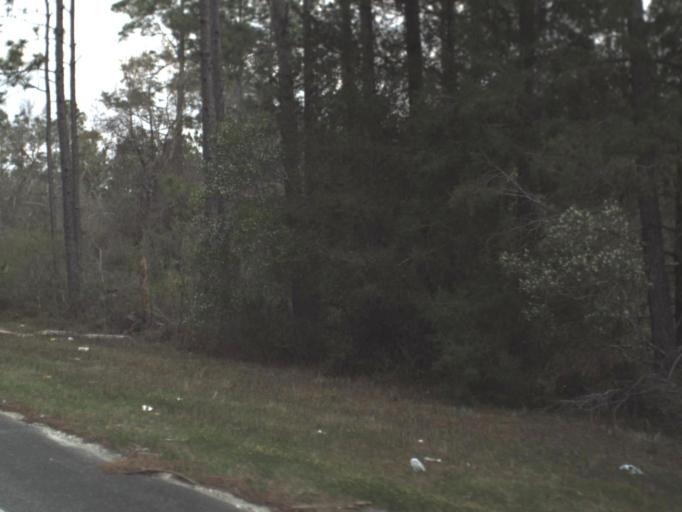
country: US
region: Florida
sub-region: Franklin County
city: Apalachicola
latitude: 29.9196
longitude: -84.9773
